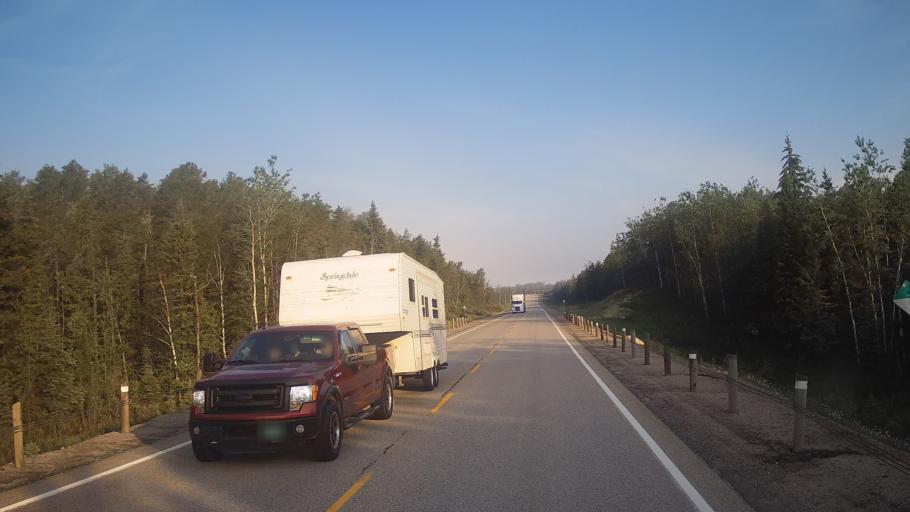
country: CA
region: Ontario
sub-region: Rainy River District
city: Atikokan
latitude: 49.3354
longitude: -91.4597
